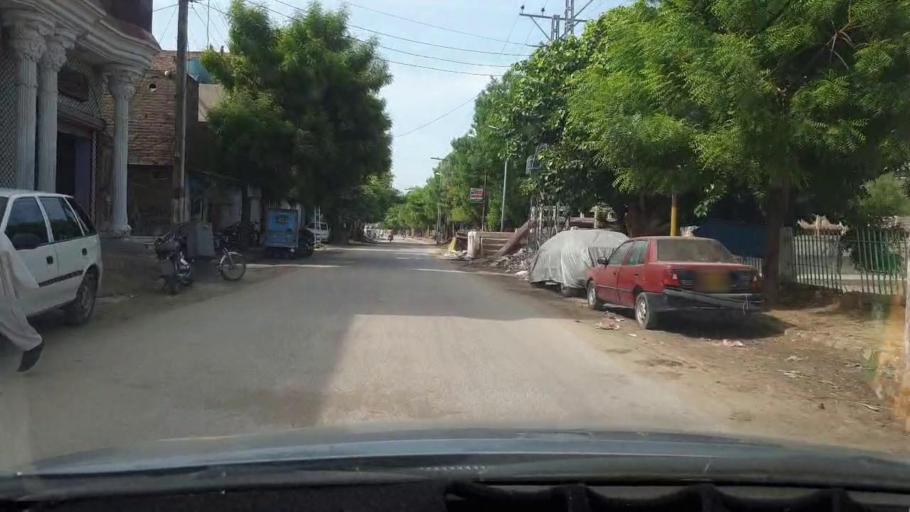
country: PK
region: Sindh
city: Khairpur
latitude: 27.5326
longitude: 68.7536
